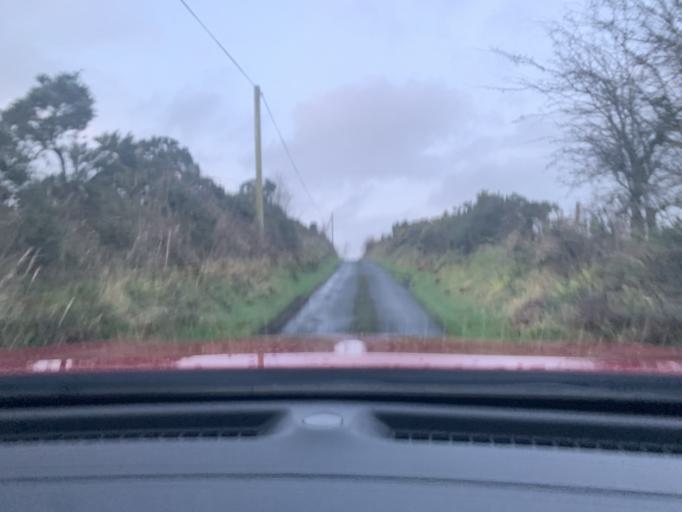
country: IE
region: Connaught
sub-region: Sligo
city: Ballymote
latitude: 54.0439
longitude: -8.4076
